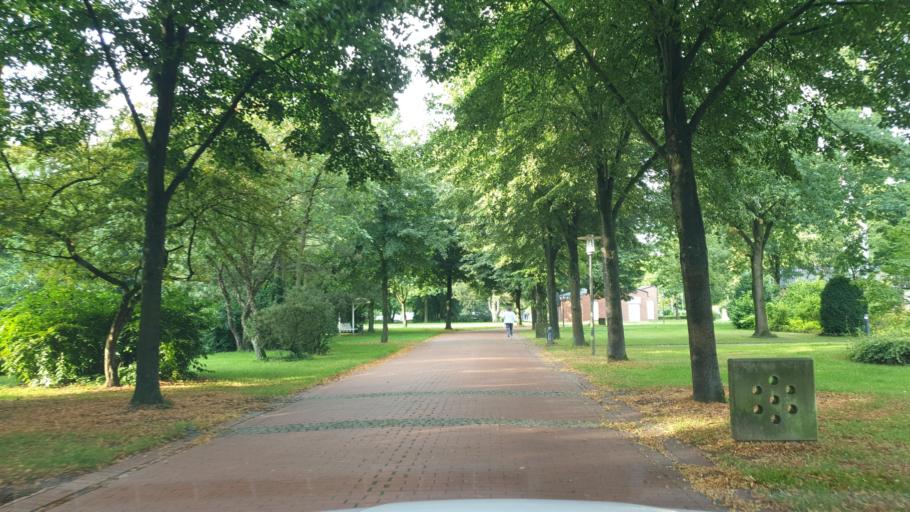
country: DE
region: North Rhine-Westphalia
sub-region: Regierungsbezirk Munster
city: Telgte
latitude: 52.0131
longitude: 7.7099
